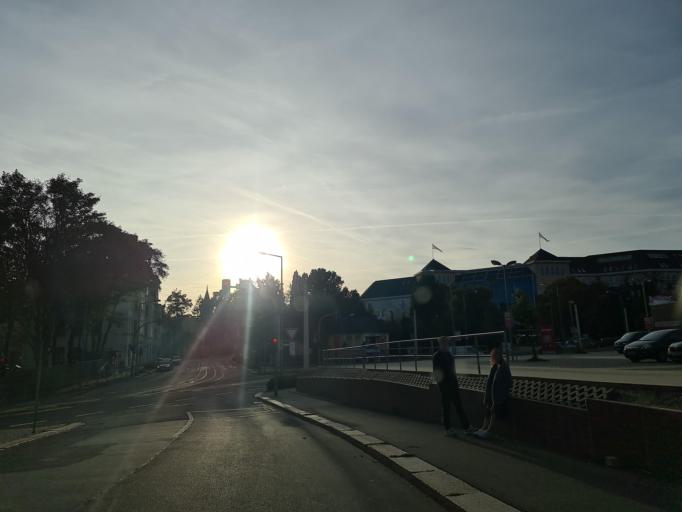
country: DE
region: Saxony
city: Plauen
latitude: 50.4946
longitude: 12.1053
